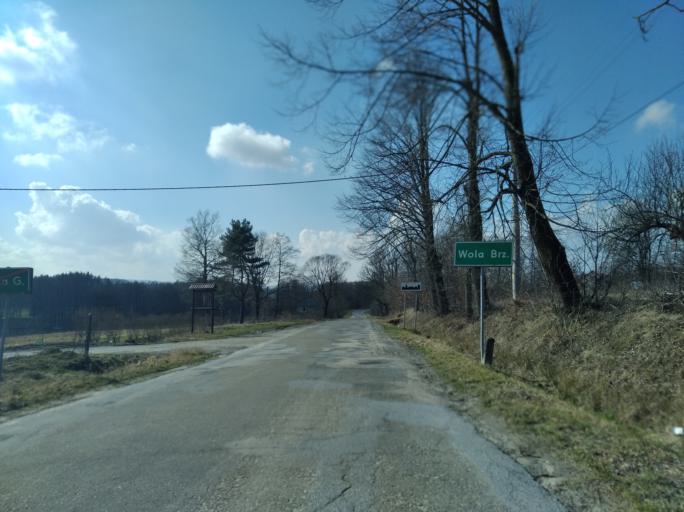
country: PL
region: Subcarpathian Voivodeship
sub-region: Powiat debicki
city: Brzostek
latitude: 49.8884
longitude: 21.4754
